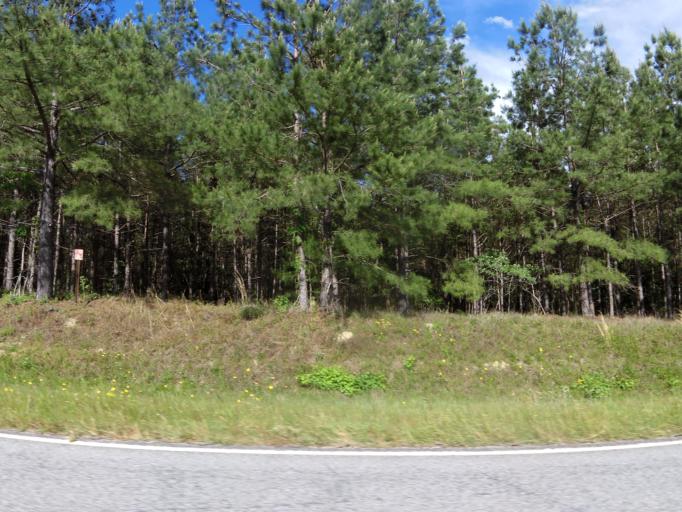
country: US
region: South Carolina
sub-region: Bamberg County
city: Denmark
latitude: 33.1516
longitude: -81.1927
